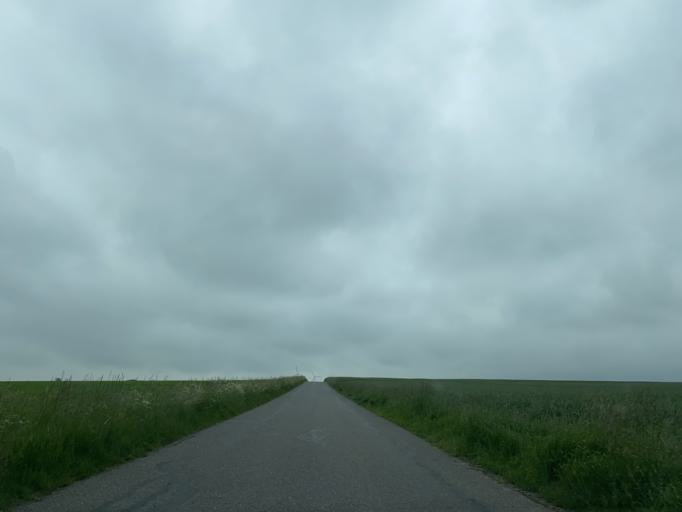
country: DK
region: Central Jutland
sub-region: Viborg Kommune
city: Bjerringbro
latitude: 56.3359
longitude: 9.6710
